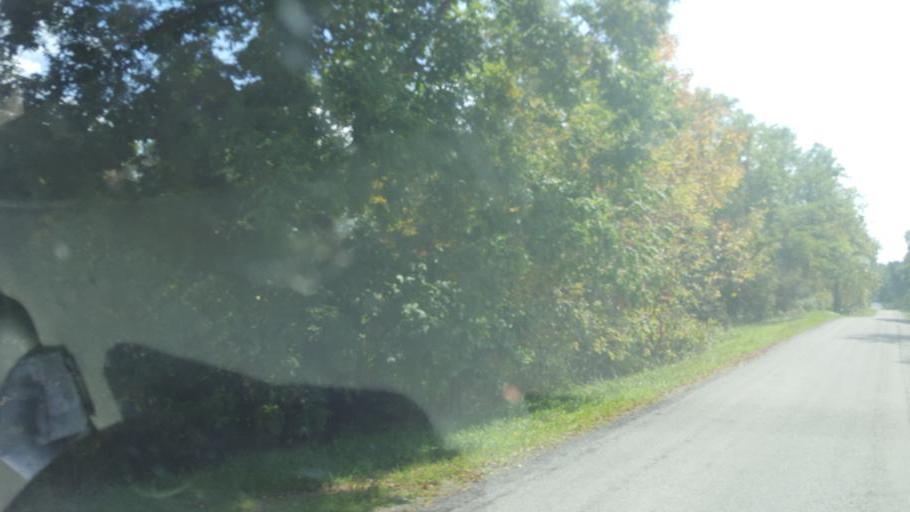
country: US
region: Ohio
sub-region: Knox County
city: Centerburg
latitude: 40.3586
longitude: -82.6354
